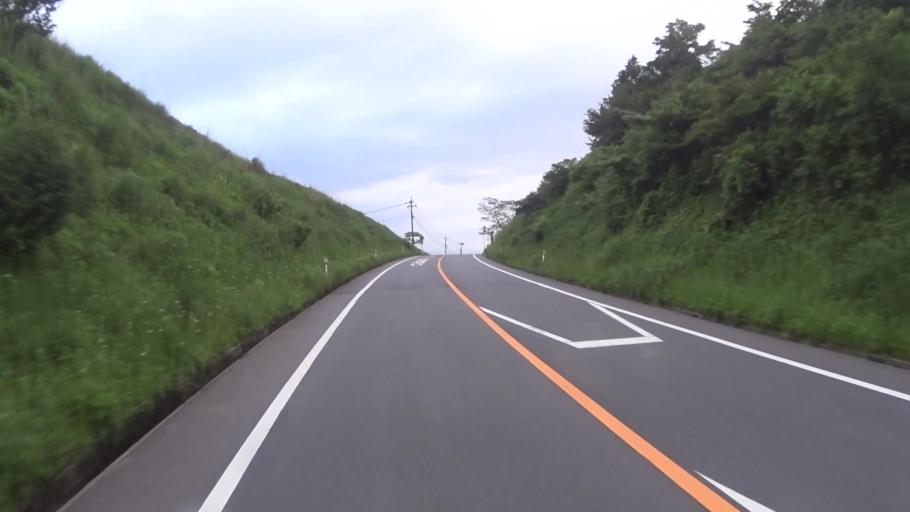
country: JP
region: Kumamoto
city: Ozu
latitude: 32.9165
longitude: 130.9653
